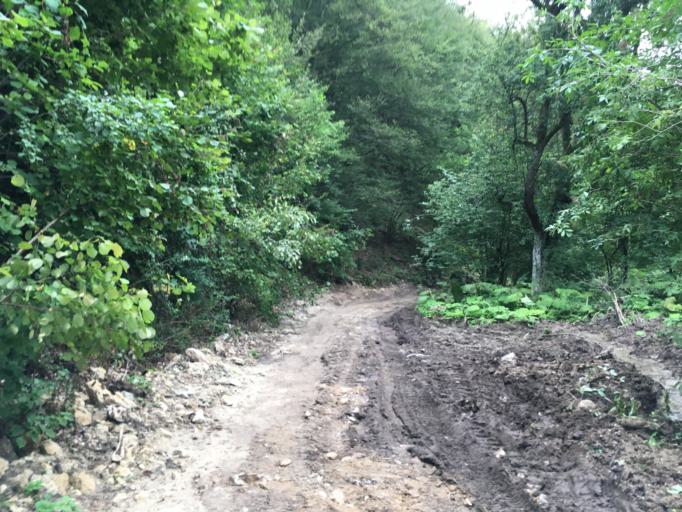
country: SK
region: Trenciansky
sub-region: Okres Povazska Bystrica
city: Povazska Bystrica
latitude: 48.9845
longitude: 18.4152
